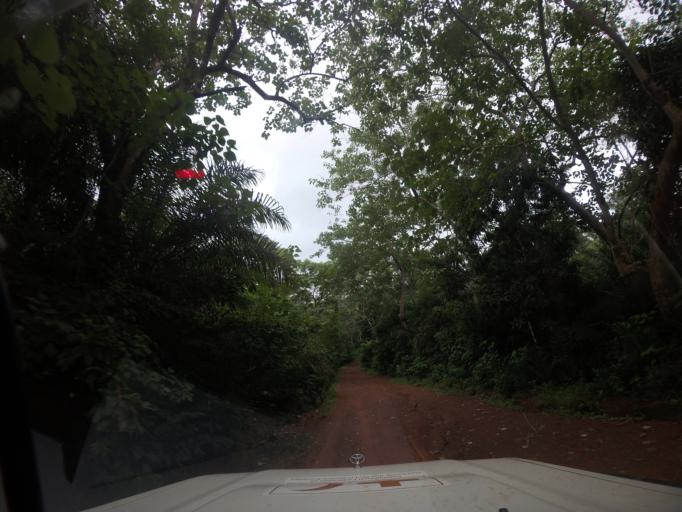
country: SL
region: Northern Province
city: Kamakwie
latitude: 9.6772
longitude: -12.2268
